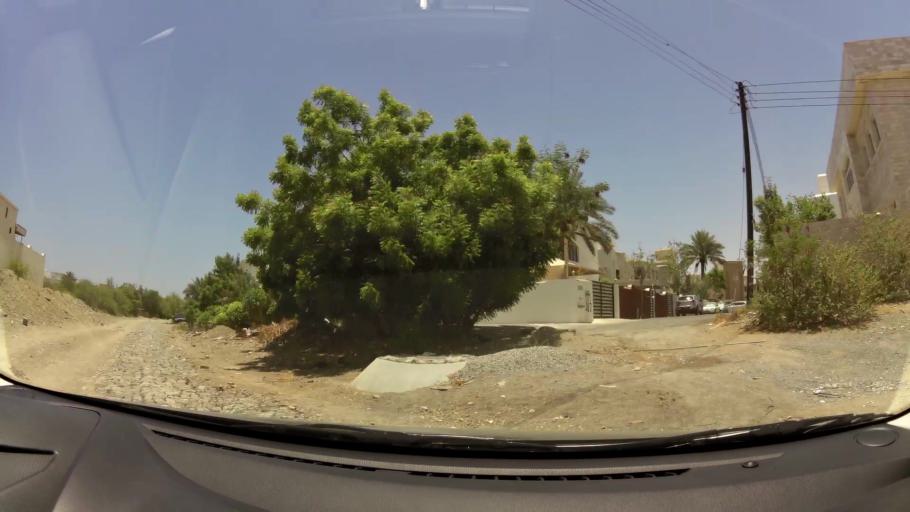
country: OM
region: Muhafazat Masqat
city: As Sib al Jadidah
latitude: 23.6315
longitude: 58.2388
